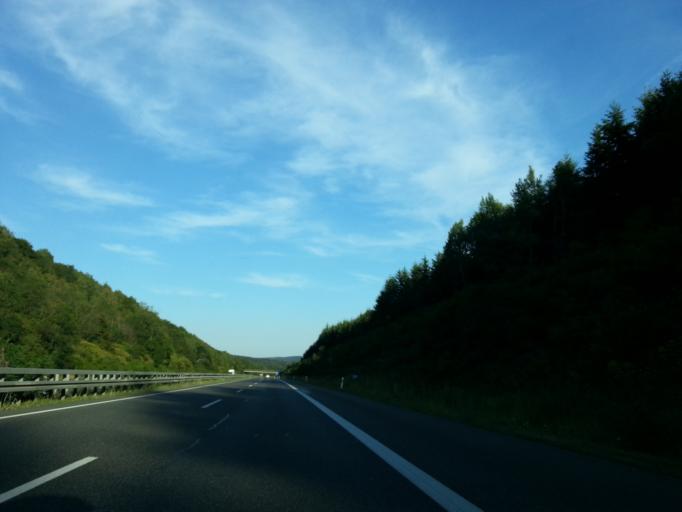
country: DE
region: Saarland
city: Nonnweiler
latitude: 49.6196
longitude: 6.9420
